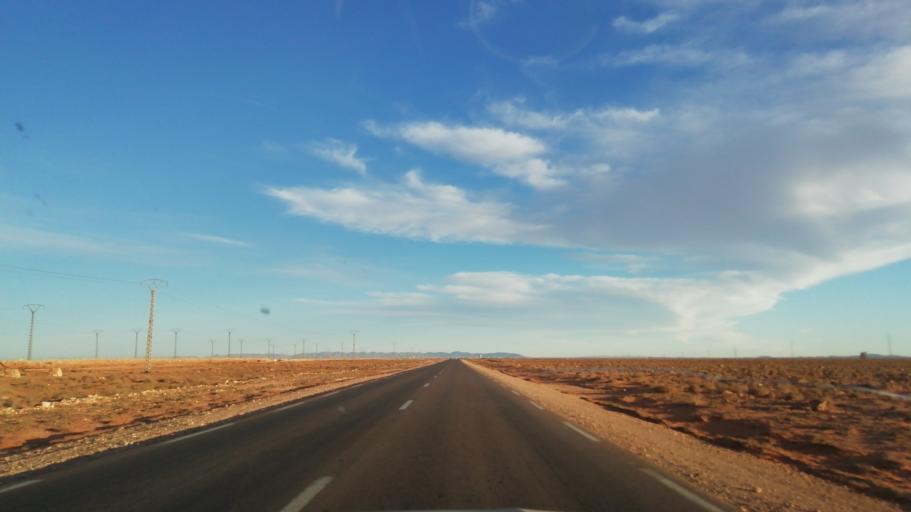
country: DZ
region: Wilaya de Naama
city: Naama
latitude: 33.7376
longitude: -0.7664
